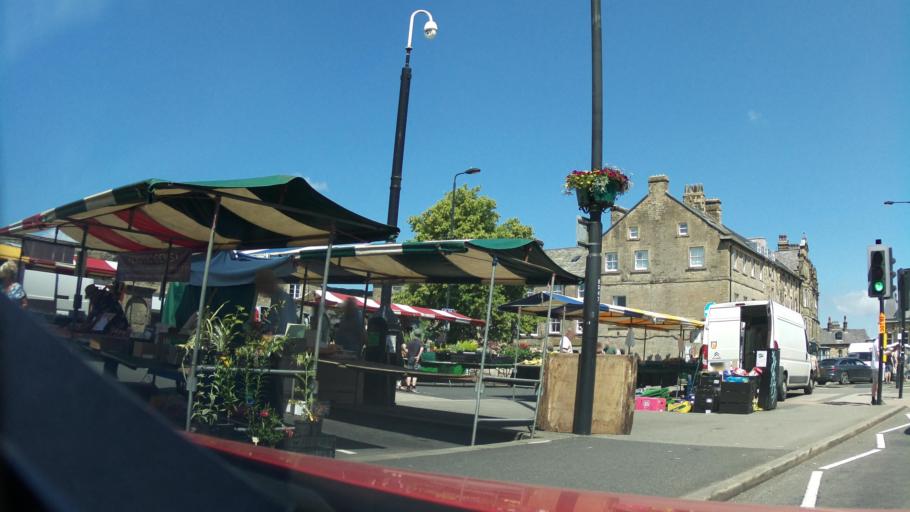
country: GB
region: England
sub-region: Derbyshire
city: Buxton
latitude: 53.2556
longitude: -1.9149
